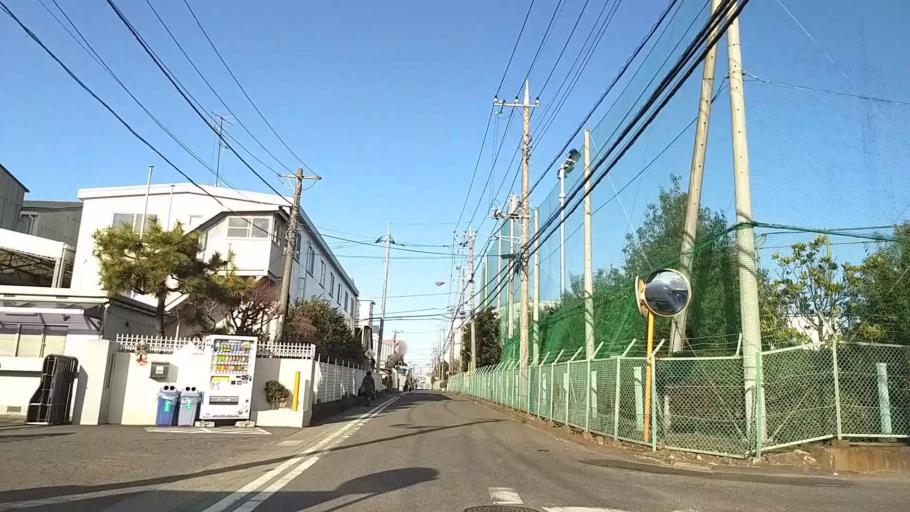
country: JP
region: Kanagawa
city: Atsugi
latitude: 35.4459
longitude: 139.3390
